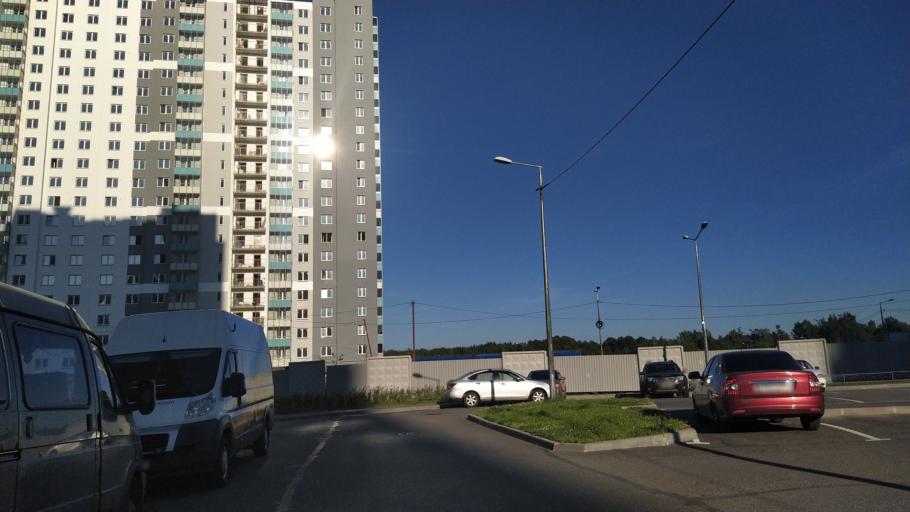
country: RU
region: Leningrad
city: Murino
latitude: 60.0327
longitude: 30.4600
